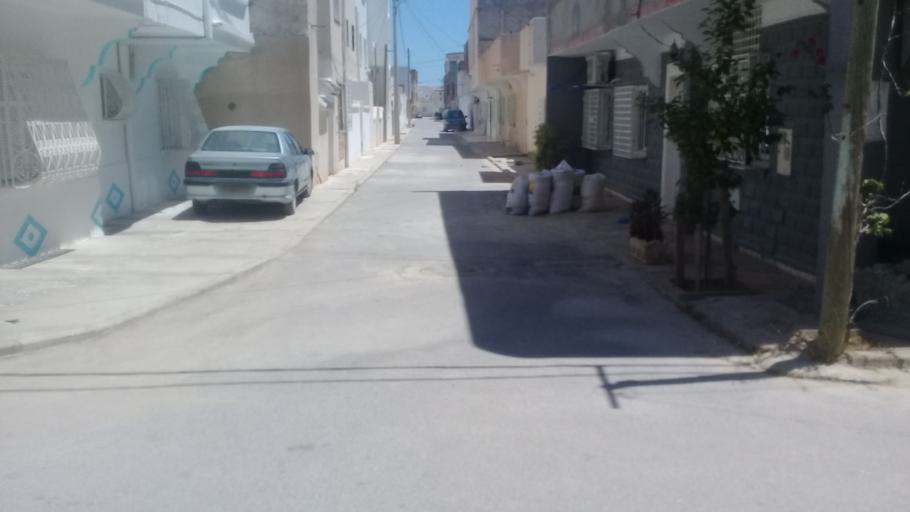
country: TN
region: Al Qayrawan
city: Kairouan
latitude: 35.6681
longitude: 10.0847
